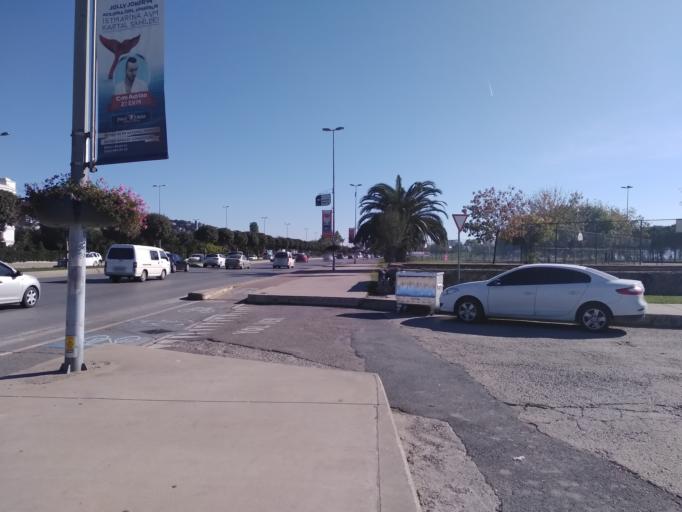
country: TR
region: Istanbul
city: Maltepe
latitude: 40.9154
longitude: 29.1320
